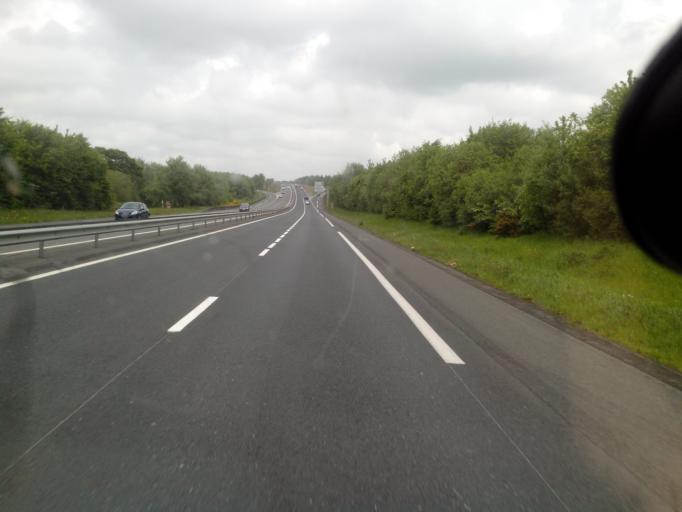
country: FR
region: Lower Normandy
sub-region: Departement du Calvados
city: Saint-Martin-des-Besaces
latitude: 49.0212
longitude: -0.8395
